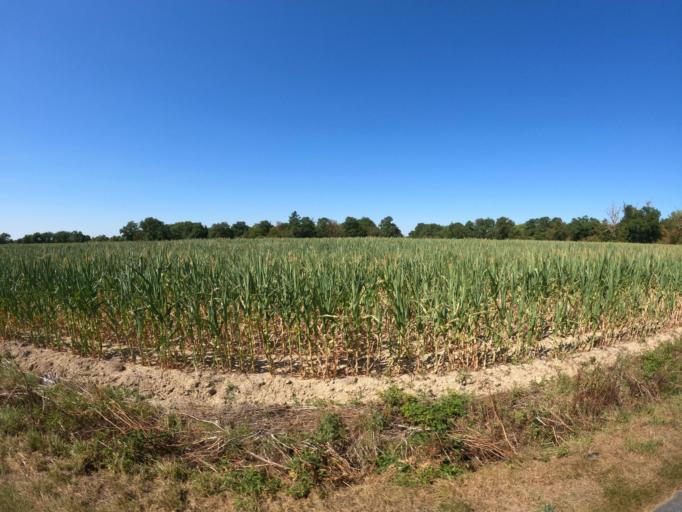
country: FR
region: Pays de la Loire
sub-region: Departement de la Vendee
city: Les Landes-Genusson
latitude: 46.9602
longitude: -1.1501
